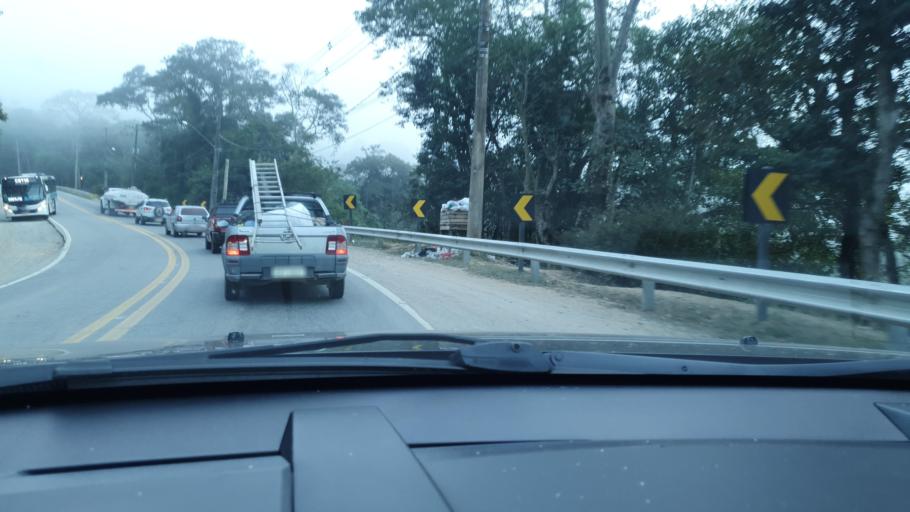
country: BR
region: Sao Paulo
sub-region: Ibiuna
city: Ibiuna
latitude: -23.6851
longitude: -47.2679
